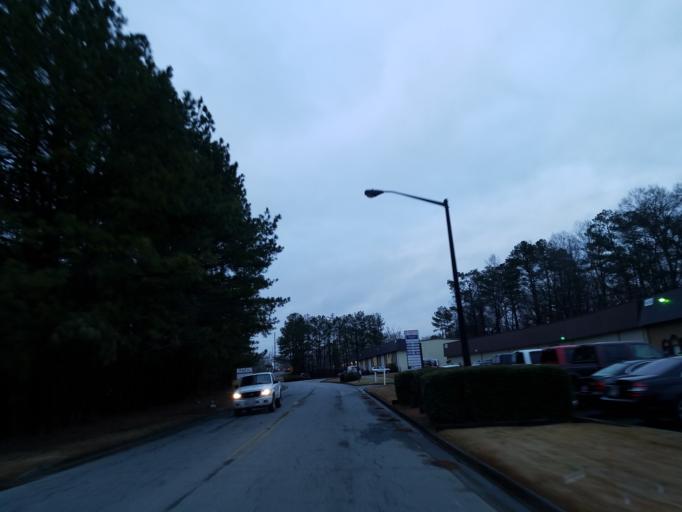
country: US
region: Georgia
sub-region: Cobb County
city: Acworth
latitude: 34.0622
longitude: -84.6605
